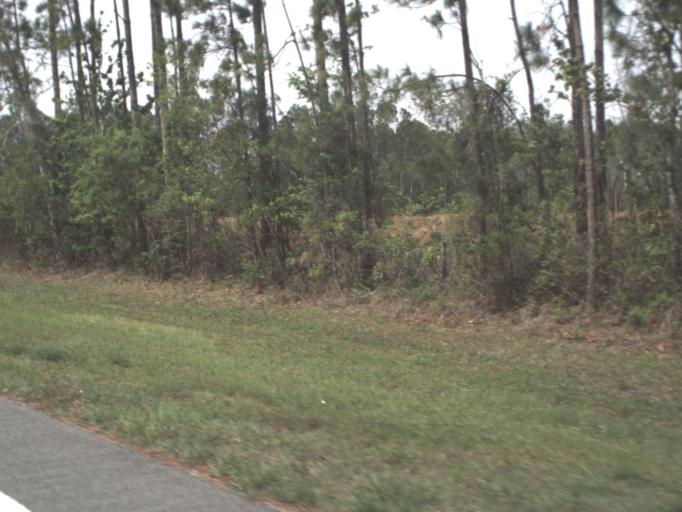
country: US
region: Florida
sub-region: Putnam County
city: Crescent City
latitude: 29.5368
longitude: -81.5202
